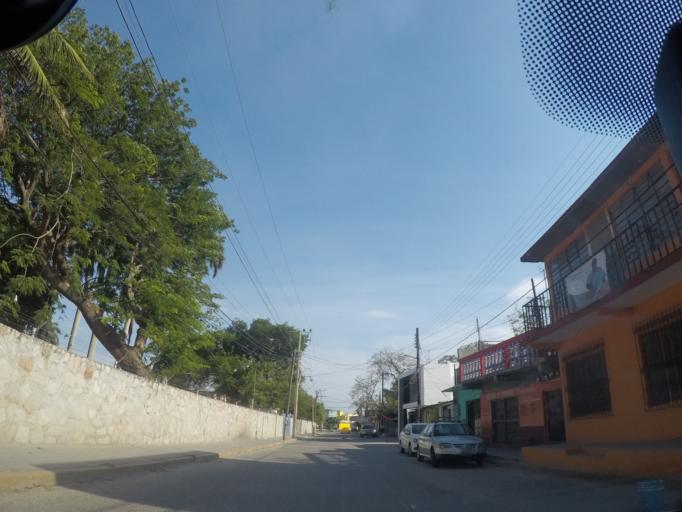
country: MX
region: Oaxaca
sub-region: Salina Cruz
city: Salina Cruz
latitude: 16.1752
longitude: -95.1978
